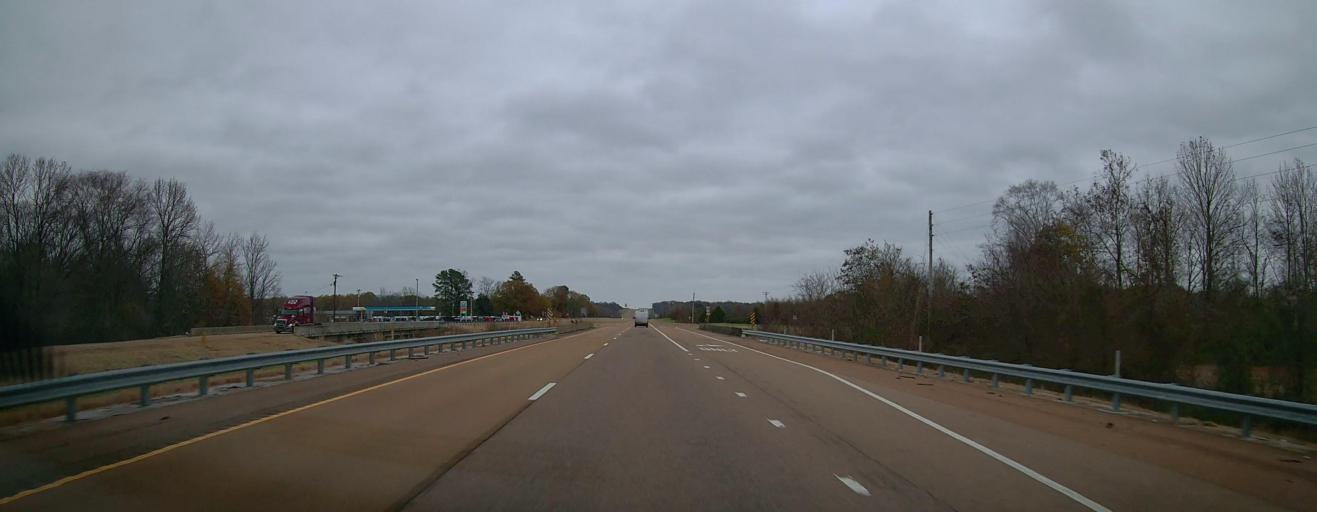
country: US
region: Mississippi
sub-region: Benton County
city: Ashland
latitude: 34.9461
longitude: -89.2136
